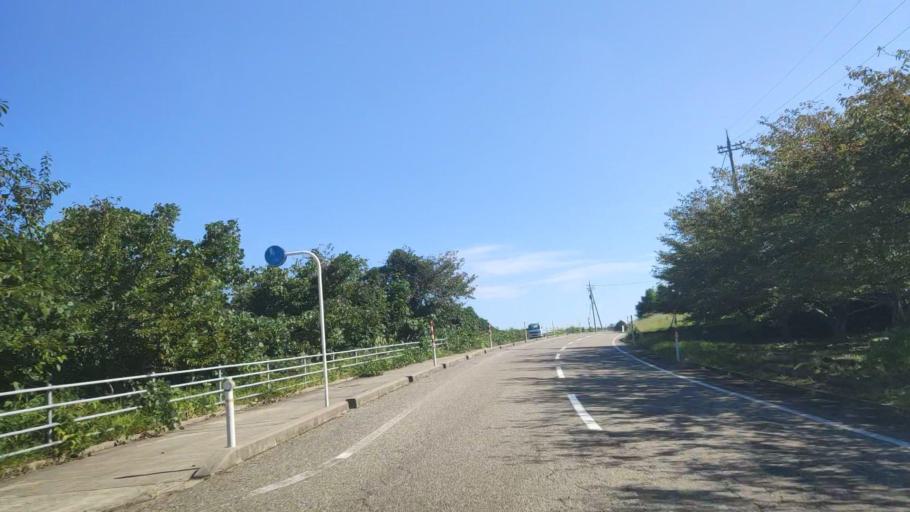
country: JP
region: Ishikawa
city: Hakui
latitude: 37.0772
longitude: 136.7241
